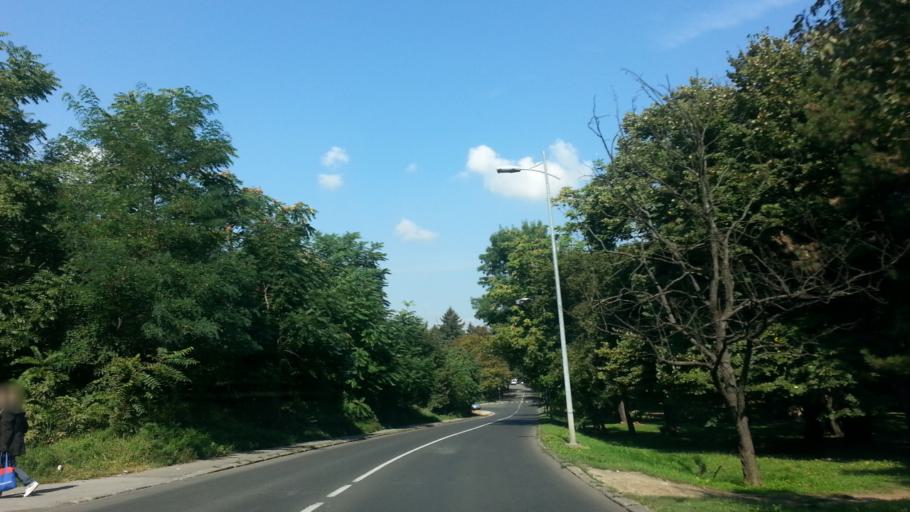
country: RS
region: Central Serbia
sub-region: Belgrade
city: Cukarica
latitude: 44.7622
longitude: 20.4300
